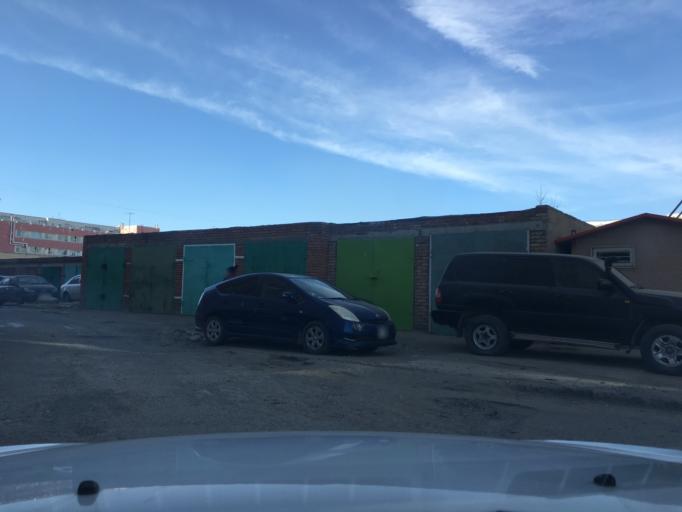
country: MN
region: Ulaanbaatar
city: Ulaanbaatar
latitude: 47.9145
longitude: 106.8486
